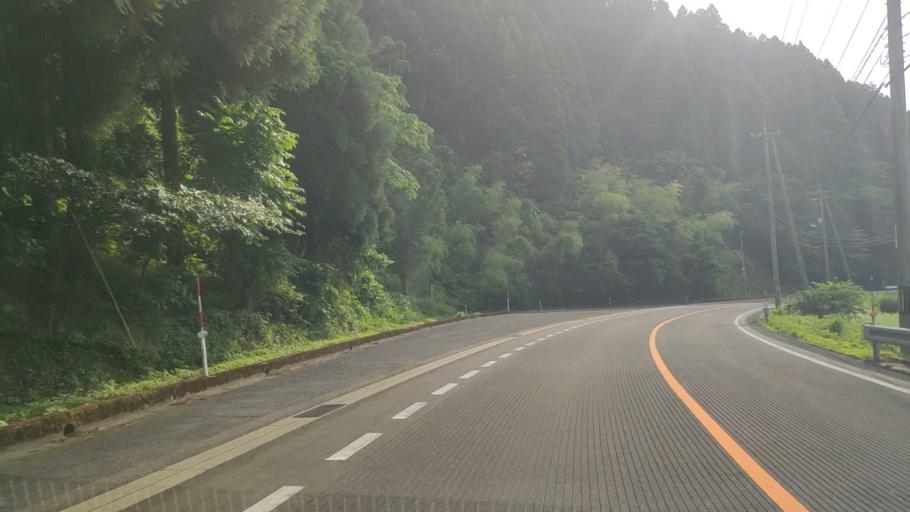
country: JP
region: Tottori
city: Kurayoshi
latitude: 35.3182
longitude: 133.8454
